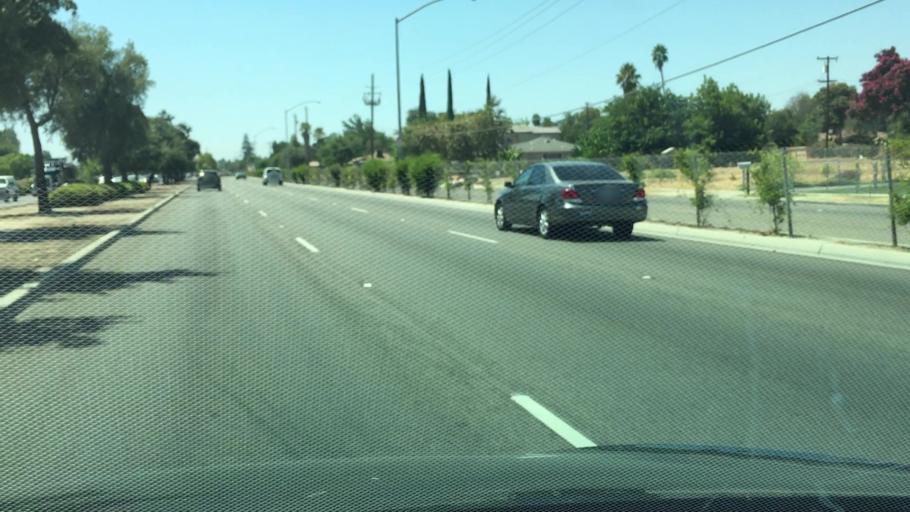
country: US
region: California
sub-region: Fresno County
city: Clovis
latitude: 36.8373
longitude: -119.7924
